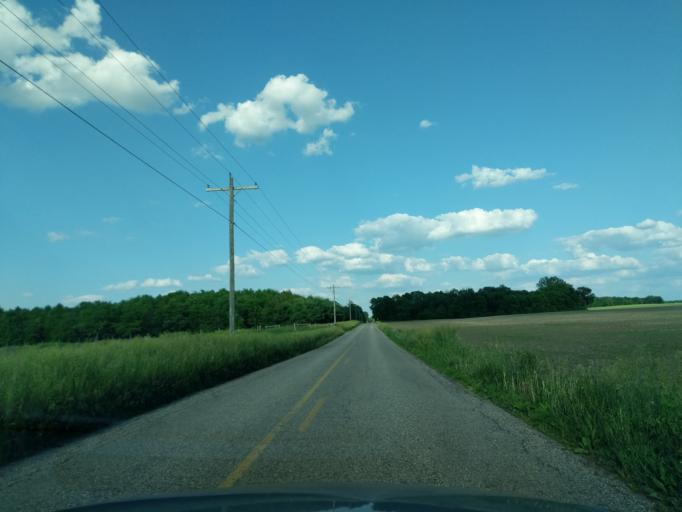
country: US
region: Indiana
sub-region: Kosciusko County
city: North Webster
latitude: 41.3025
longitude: -85.6053
